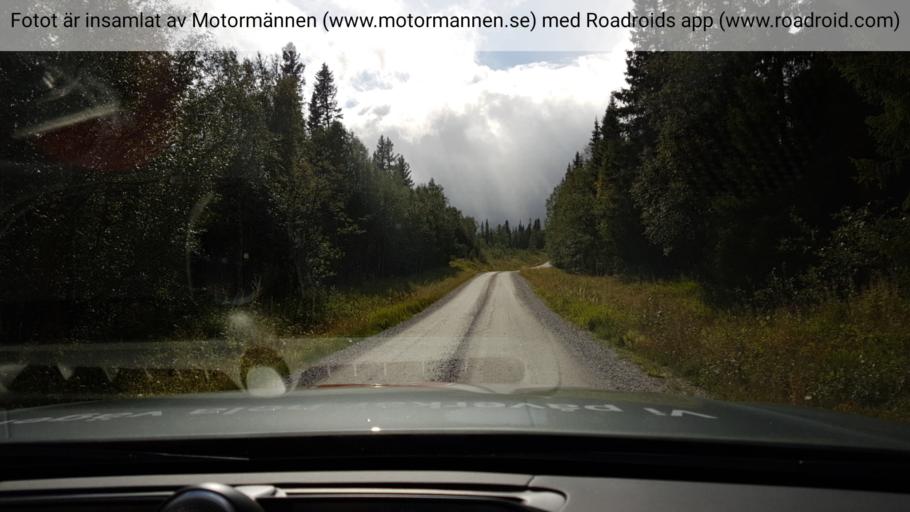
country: SE
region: Jaemtland
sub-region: Krokoms Kommun
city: Valla
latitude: 63.8793
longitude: 14.1361
